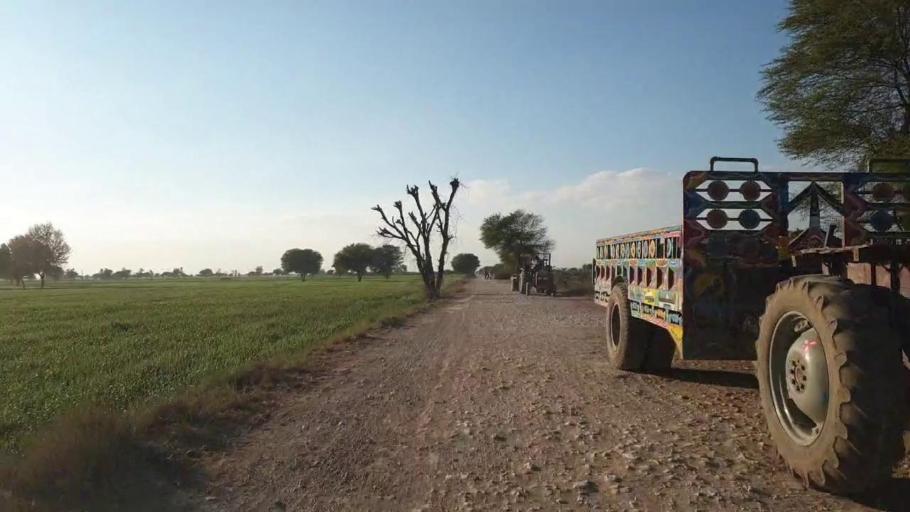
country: PK
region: Sindh
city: Shahpur Chakar
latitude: 26.1381
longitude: 68.5551
